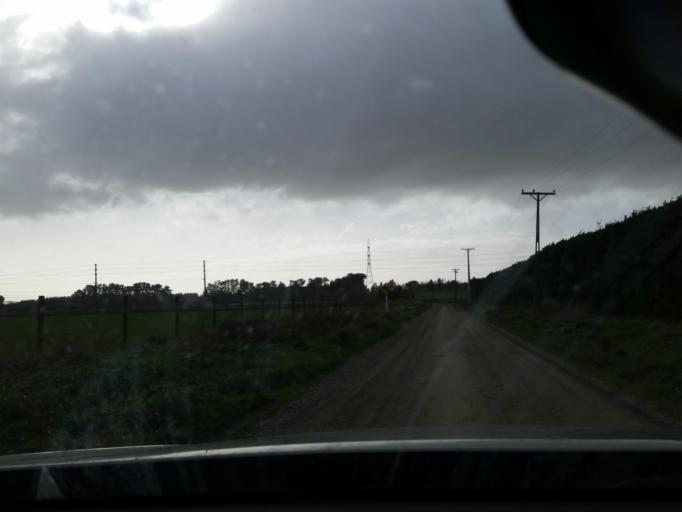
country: NZ
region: Southland
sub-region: Invercargill City
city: Invercargill
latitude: -46.3094
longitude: 168.3662
